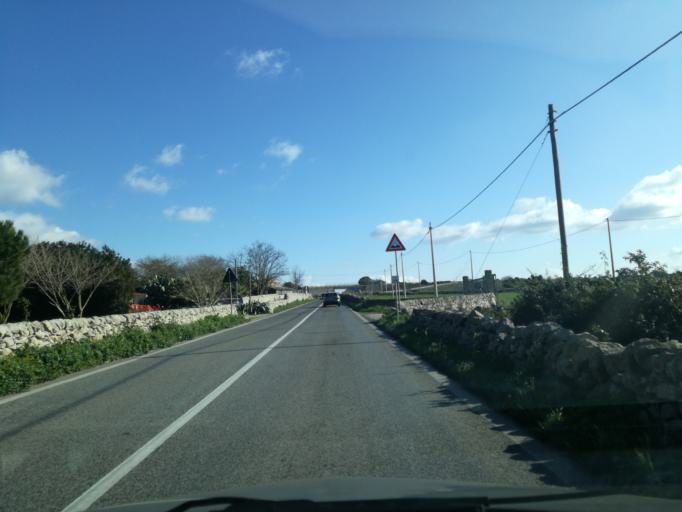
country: IT
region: Sicily
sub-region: Ragusa
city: Comiso
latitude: 36.9399
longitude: 14.6463
